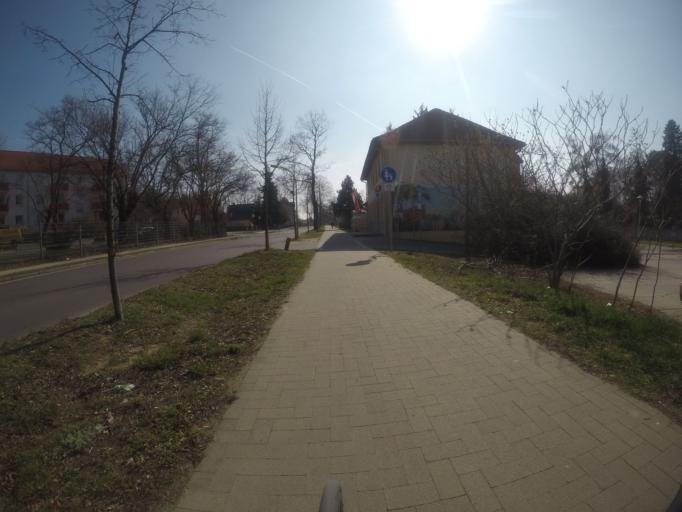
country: DE
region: Brandenburg
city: Konigs Wusterhausen
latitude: 52.3076
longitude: 13.6481
